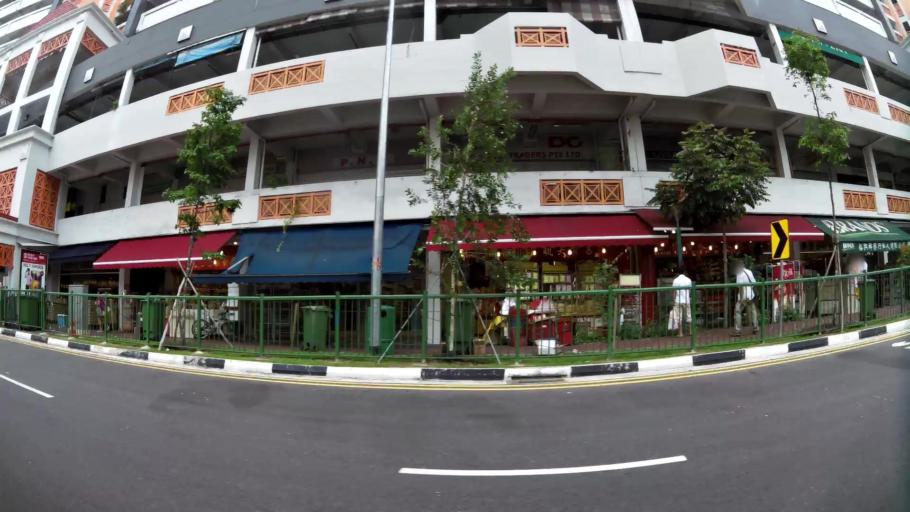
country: SG
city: Singapore
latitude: 1.2863
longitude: 103.8424
